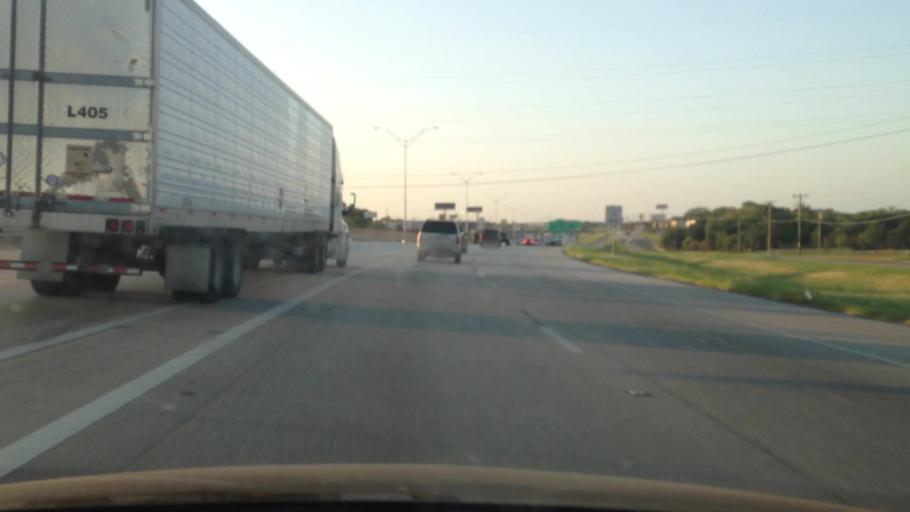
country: US
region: Texas
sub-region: Tarrant County
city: Forest Hill
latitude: 32.6736
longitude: -97.2404
